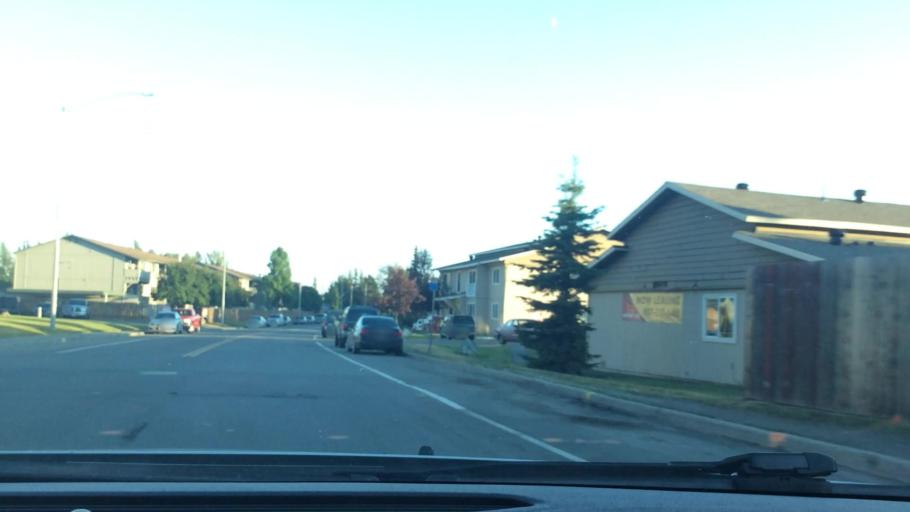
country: US
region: Alaska
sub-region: Anchorage Municipality
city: Anchorage
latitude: 61.2230
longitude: -149.7919
